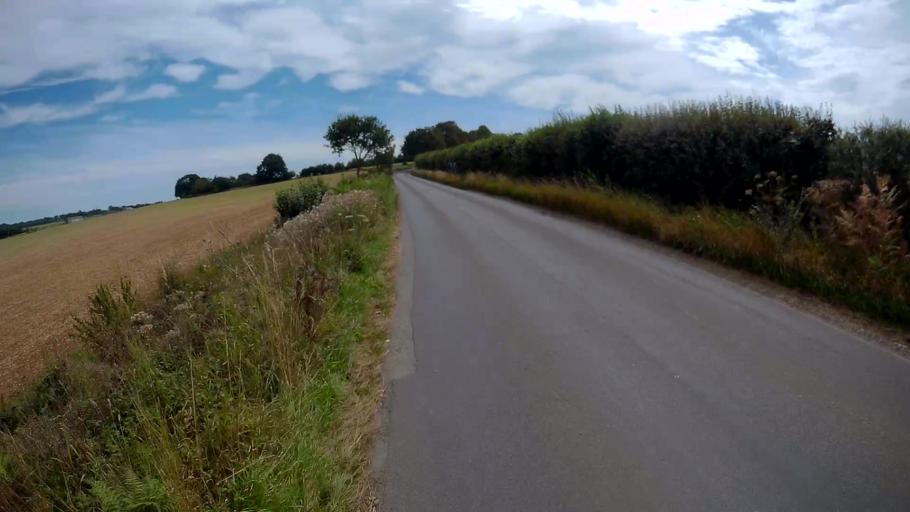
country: GB
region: England
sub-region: Hampshire
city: Long Sutton
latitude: 51.2291
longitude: -0.9583
